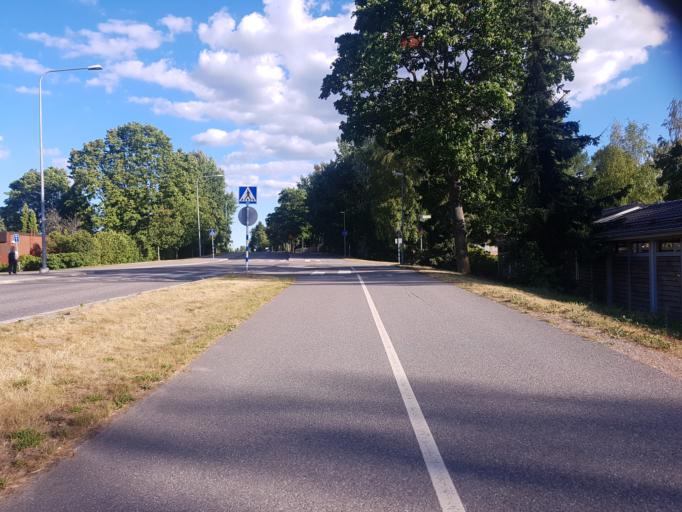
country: FI
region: Uusimaa
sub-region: Helsinki
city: Vantaa
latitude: 60.2622
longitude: 24.9848
